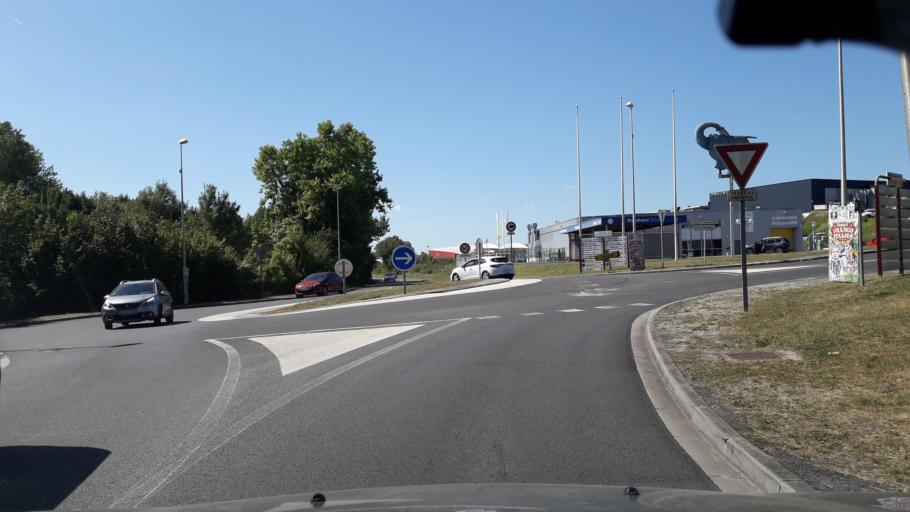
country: FR
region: Poitou-Charentes
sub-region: Departement de la Charente
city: Gond-Pontouvre
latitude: 45.6857
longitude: 0.1833
